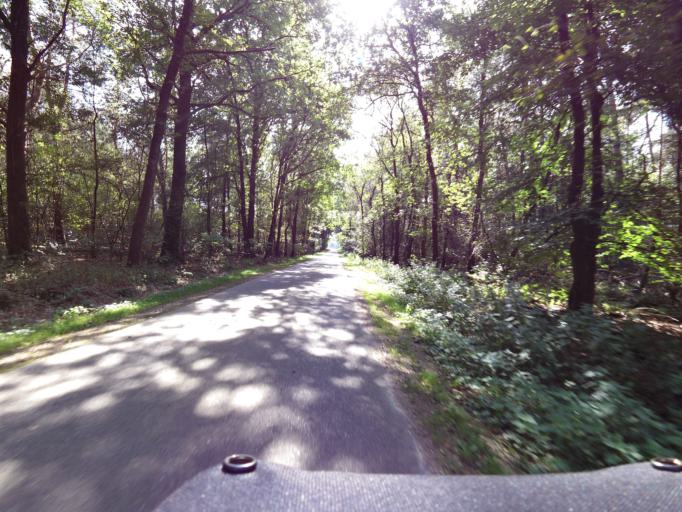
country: NL
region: Gelderland
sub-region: Gemeente Barneveld
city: Garderen
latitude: 52.2174
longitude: 5.7573
